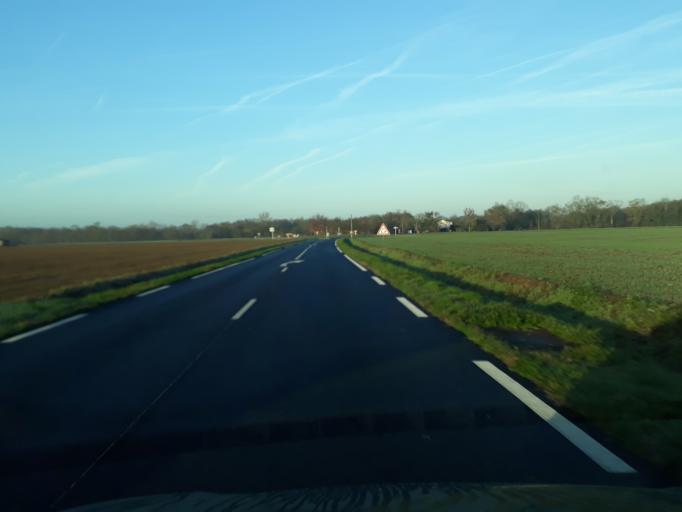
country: FR
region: Midi-Pyrenees
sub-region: Departement de la Haute-Garonne
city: Longages
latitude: 43.3576
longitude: 1.2235
